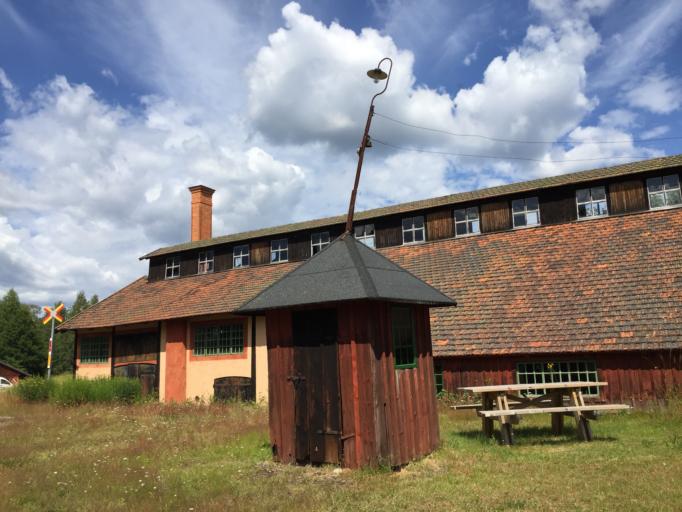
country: SE
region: Vaestmanland
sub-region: Surahammars Kommun
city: Ramnas
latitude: 59.7804
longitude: 16.1832
